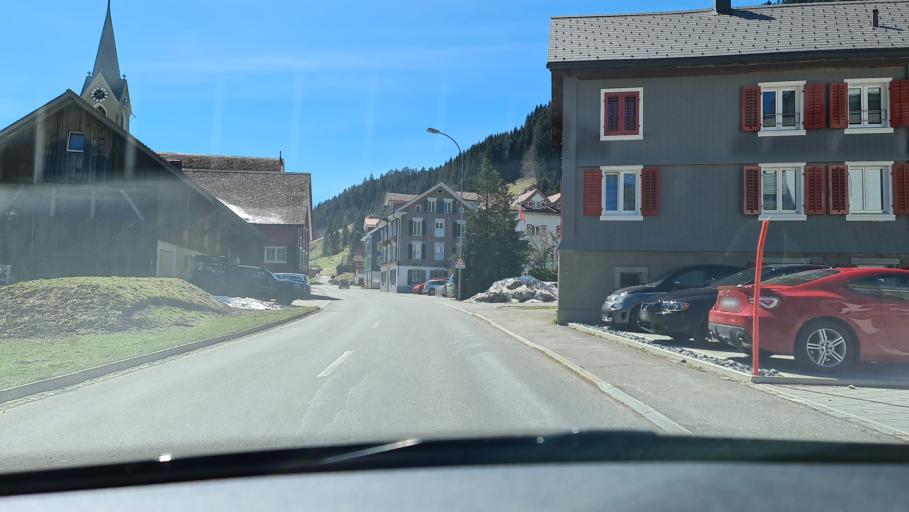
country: CH
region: Schwyz
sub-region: Bezirk Schwyz
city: Rothenthurm
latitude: 47.0718
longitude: 8.7166
